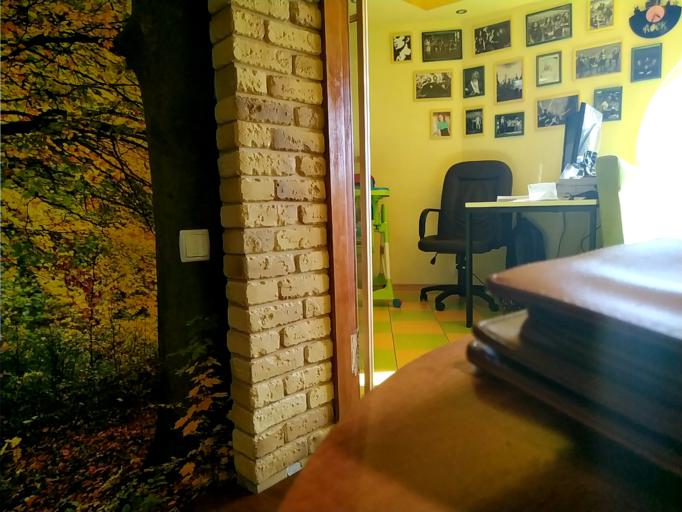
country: RU
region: Vologda
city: Nelazskoye
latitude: 59.4232
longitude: 37.6080
